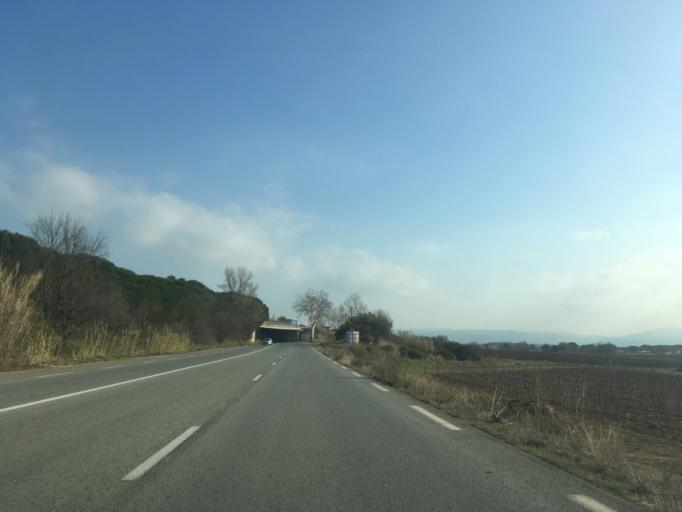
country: FR
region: Provence-Alpes-Cote d'Azur
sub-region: Departement du Var
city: Le Cannet-des-Maures
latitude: 43.4012
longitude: 6.3793
